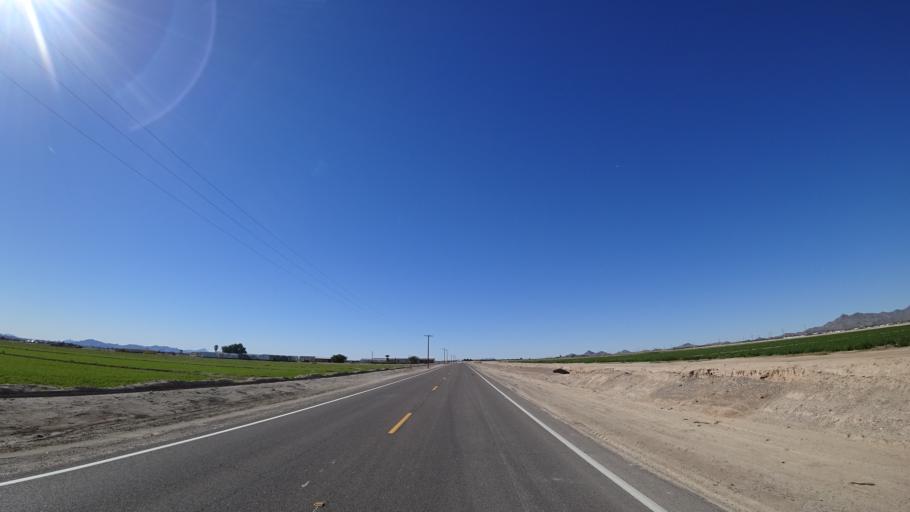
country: US
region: Arizona
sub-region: Maricopa County
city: Buckeye
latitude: 33.4069
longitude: -112.5233
